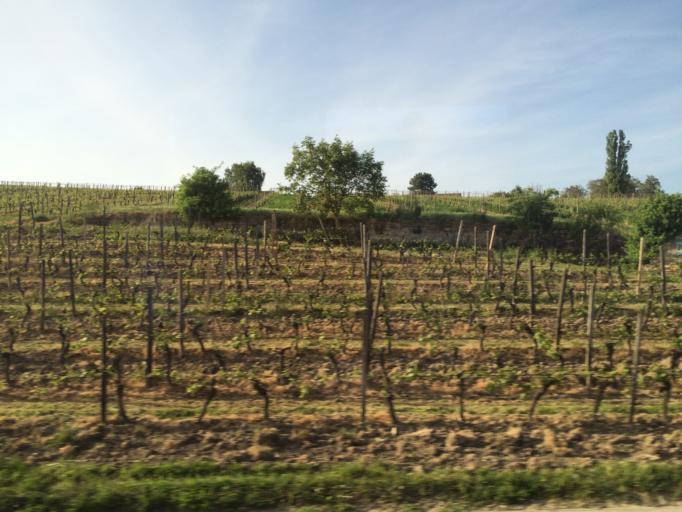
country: DE
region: Hesse
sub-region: Regierungsbezirk Darmstadt
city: Kiedrich
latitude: 50.0191
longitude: 8.0864
